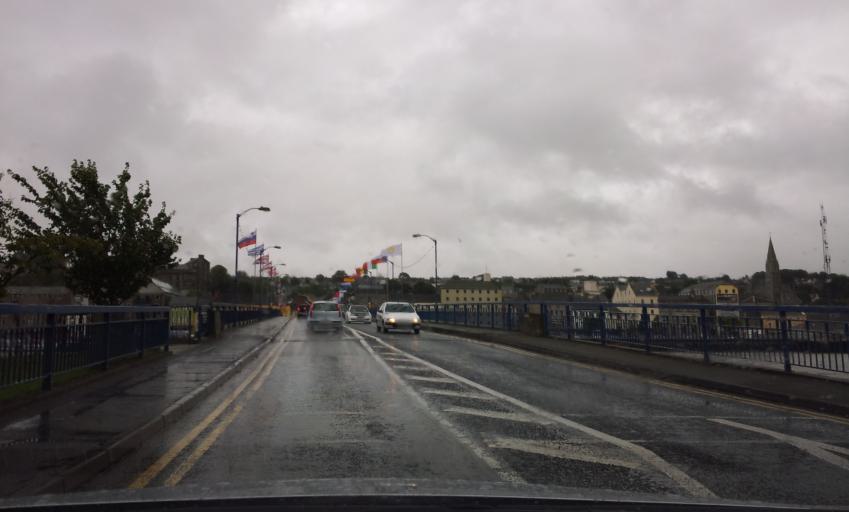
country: IE
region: Leinster
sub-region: Loch Garman
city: New Ross
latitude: 52.3965
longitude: -6.9484
